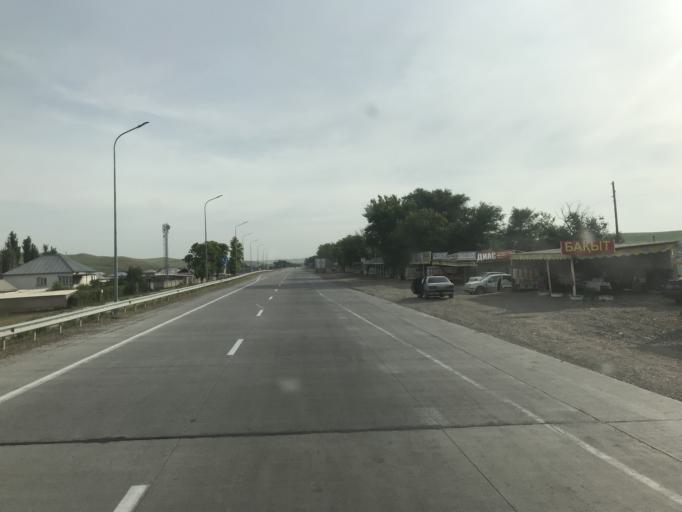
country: KZ
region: Ongtustik Qazaqstan
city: Qazyqurt
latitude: 41.9037
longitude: 69.4632
